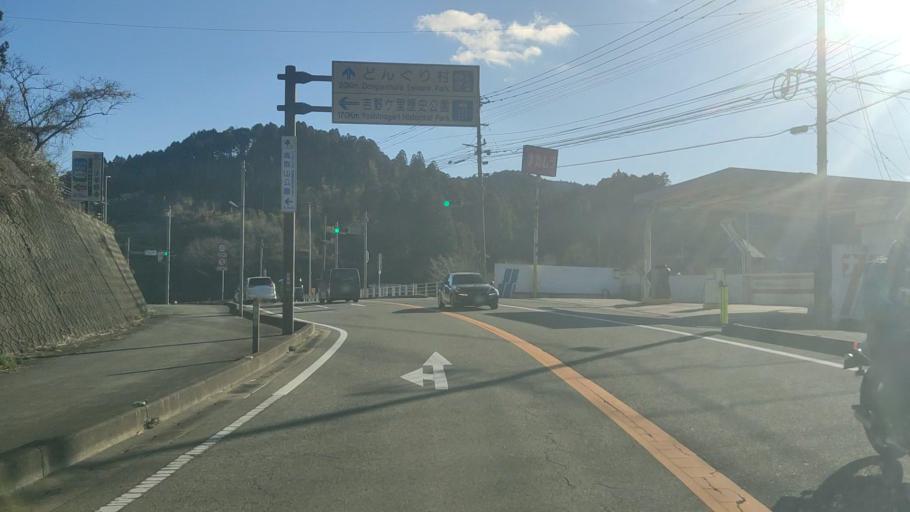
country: JP
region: Saga Prefecture
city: Kanzakimachi-kanzaki
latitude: 33.4230
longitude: 130.2773
